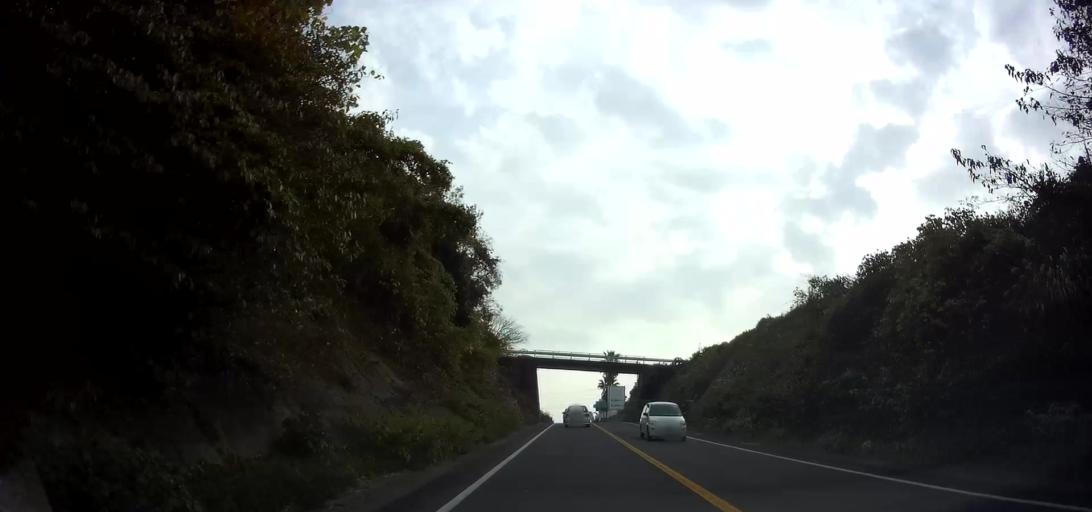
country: JP
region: Nagasaki
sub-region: Isahaya-shi
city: Isahaya
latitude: 32.7955
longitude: 130.0961
